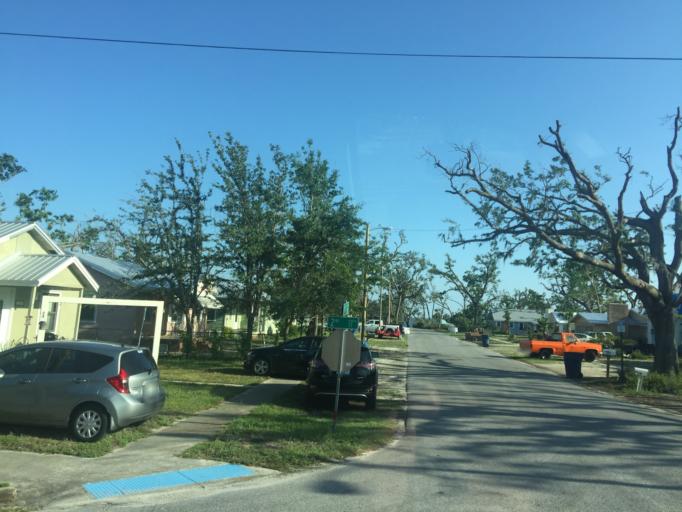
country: US
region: Florida
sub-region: Bay County
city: Panama City
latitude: 30.1477
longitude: -85.6534
